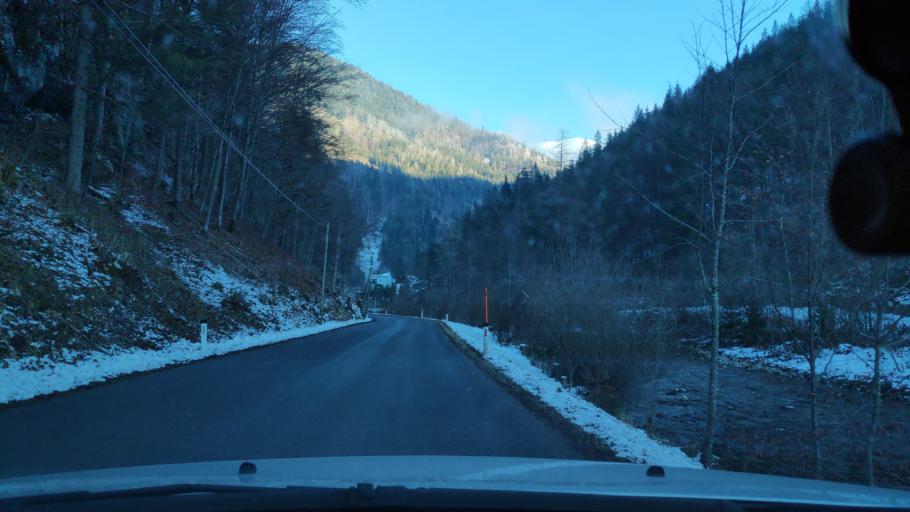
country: AT
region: Lower Austria
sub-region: Politischer Bezirk Neunkirchen
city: Schwarzau im Gebirge
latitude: 47.7714
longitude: 15.7270
